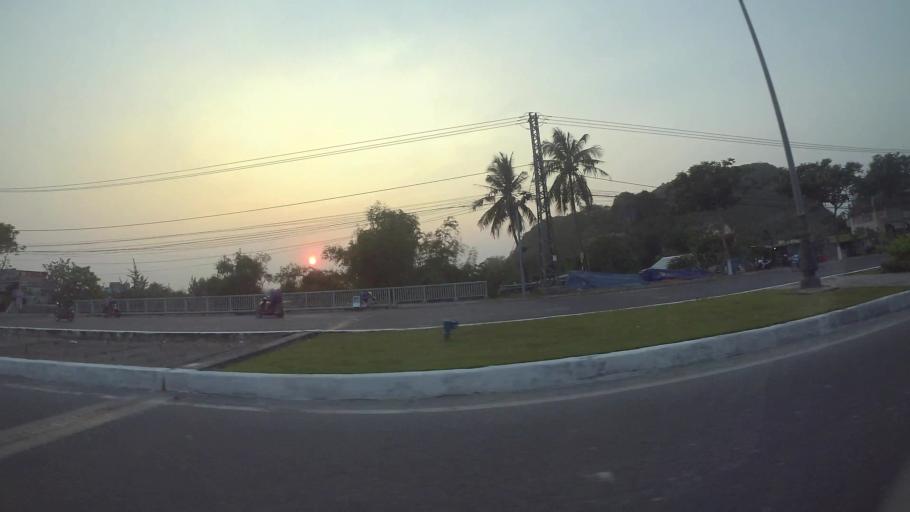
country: VN
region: Da Nang
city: Ngu Hanh Son
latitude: 15.9968
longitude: 108.2592
